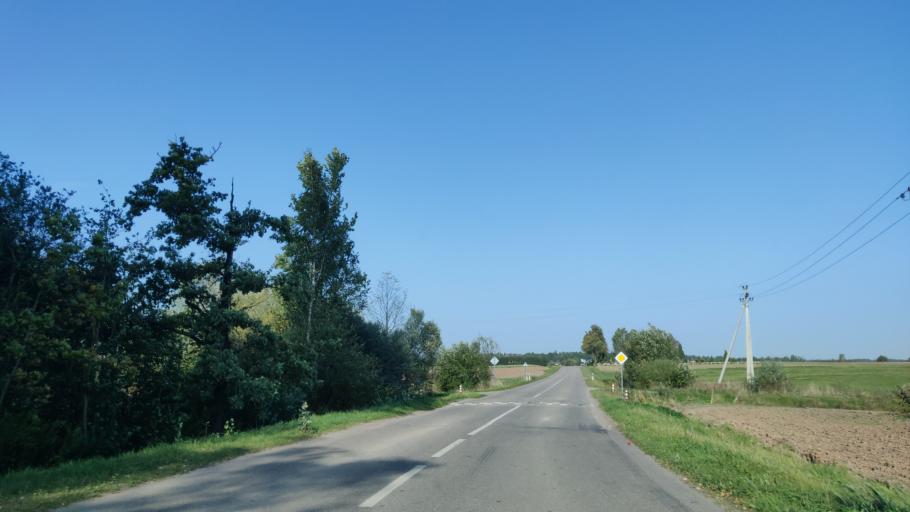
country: LT
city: Sirvintos
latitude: 54.9519
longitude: 24.8377
